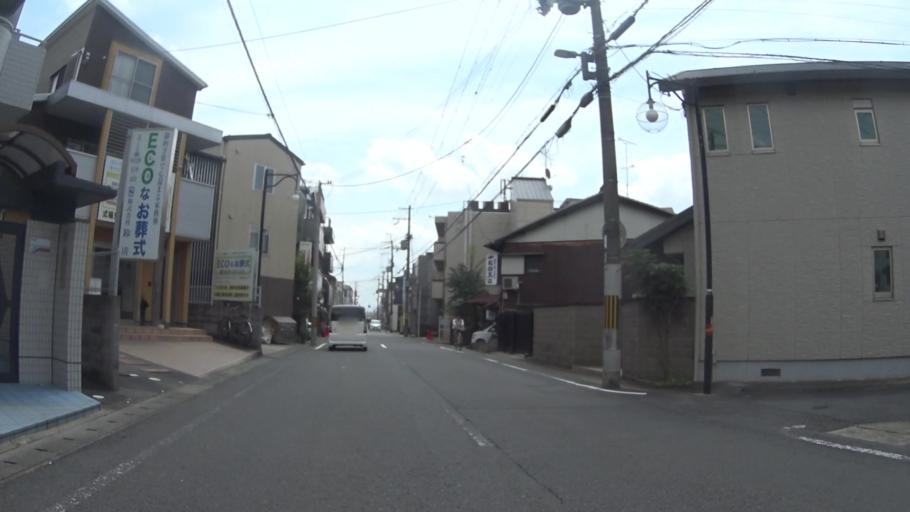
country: JP
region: Kyoto
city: Kyoto
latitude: 35.0133
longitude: 135.7117
